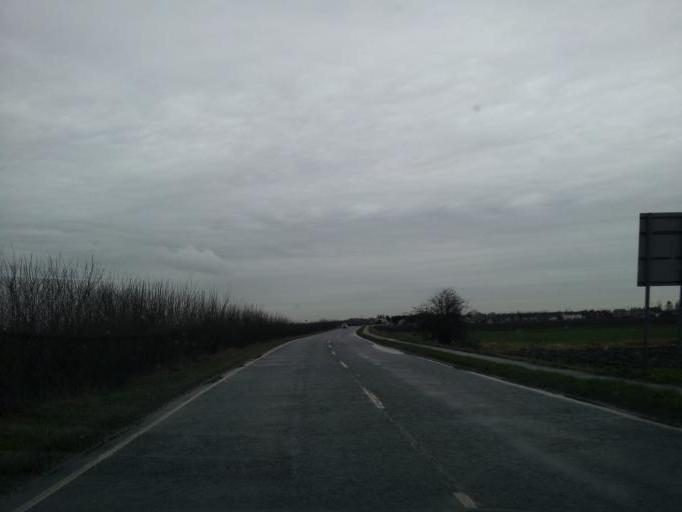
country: GB
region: England
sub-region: Cambridgeshire
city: Bottisham
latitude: 52.2416
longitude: 0.2689
